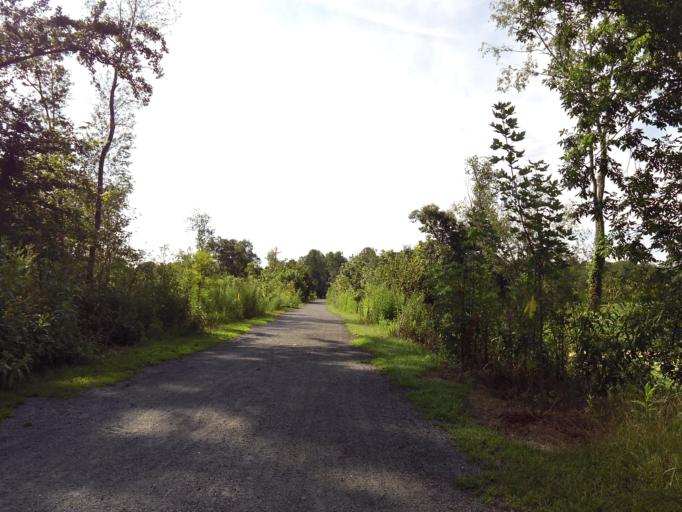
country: US
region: Virginia
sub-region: Washington County
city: Abingdon
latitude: 36.6983
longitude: -81.9524
